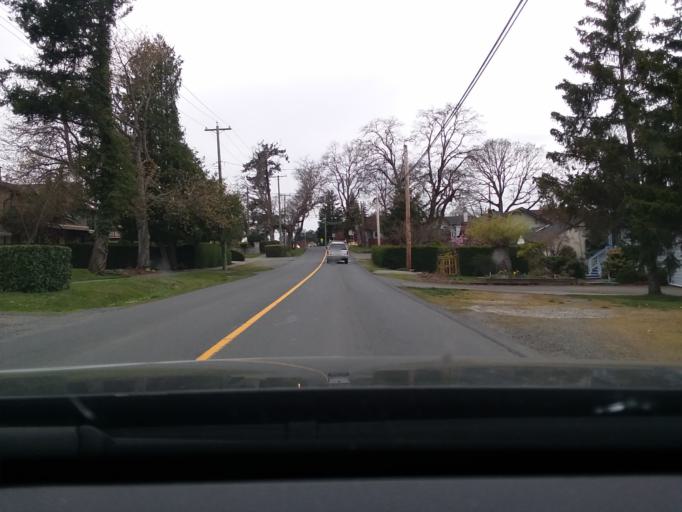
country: CA
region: British Columbia
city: Victoria
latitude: 48.4788
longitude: -123.4134
